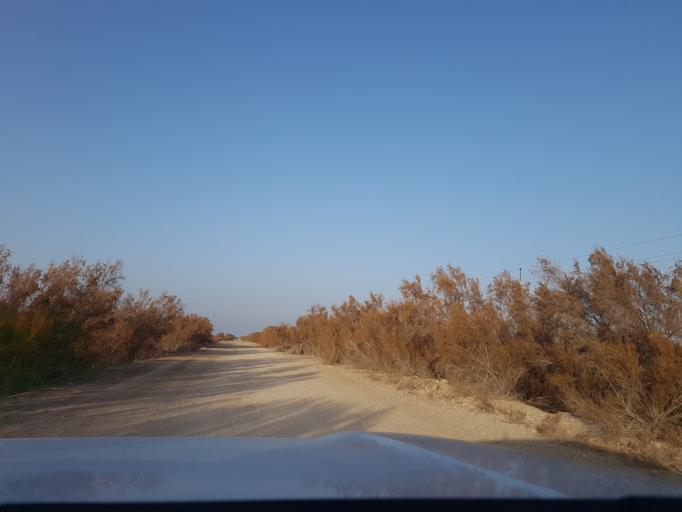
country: TM
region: Dasoguz
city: Koeneuergench
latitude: 41.8527
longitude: 58.2611
